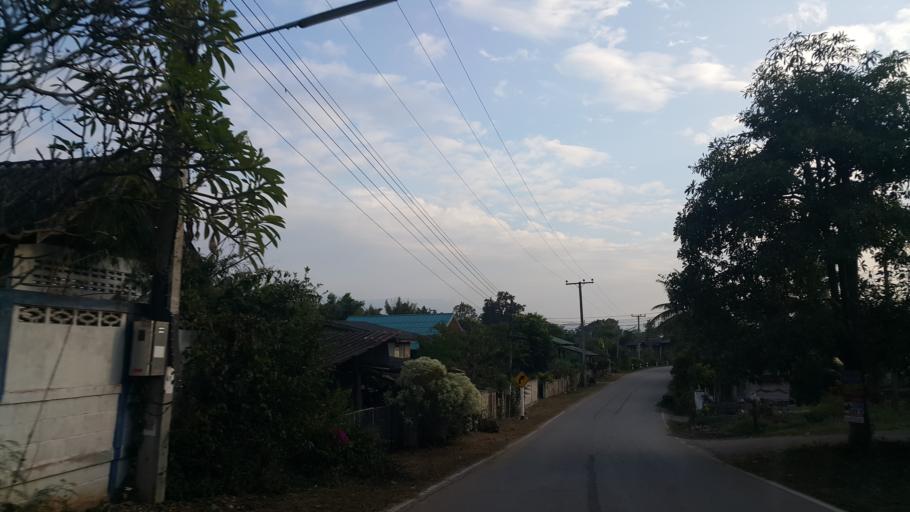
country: TH
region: Lampang
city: Sop Prap
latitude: 17.9059
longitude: 99.3298
